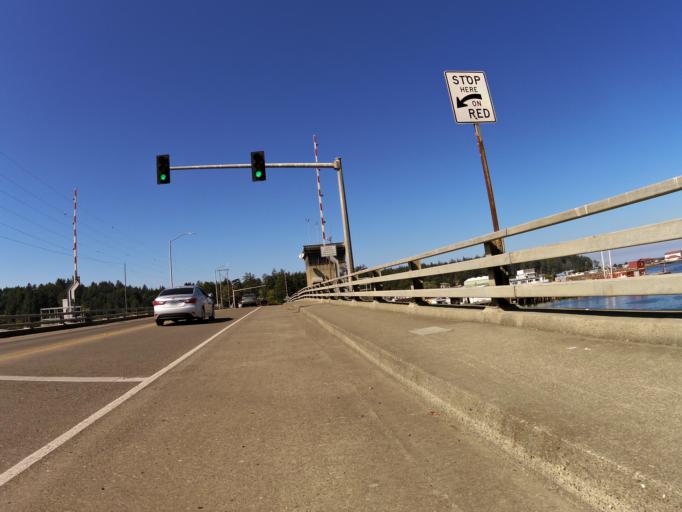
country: US
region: Oregon
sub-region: Coos County
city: Barview
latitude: 43.3388
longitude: -124.3203
